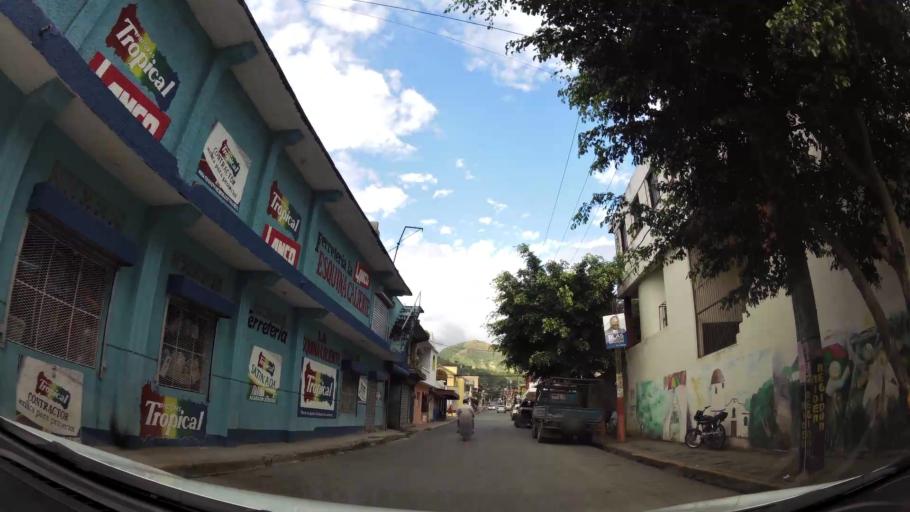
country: DO
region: San Cristobal
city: Villa Altagracia
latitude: 18.6725
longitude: -70.1746
